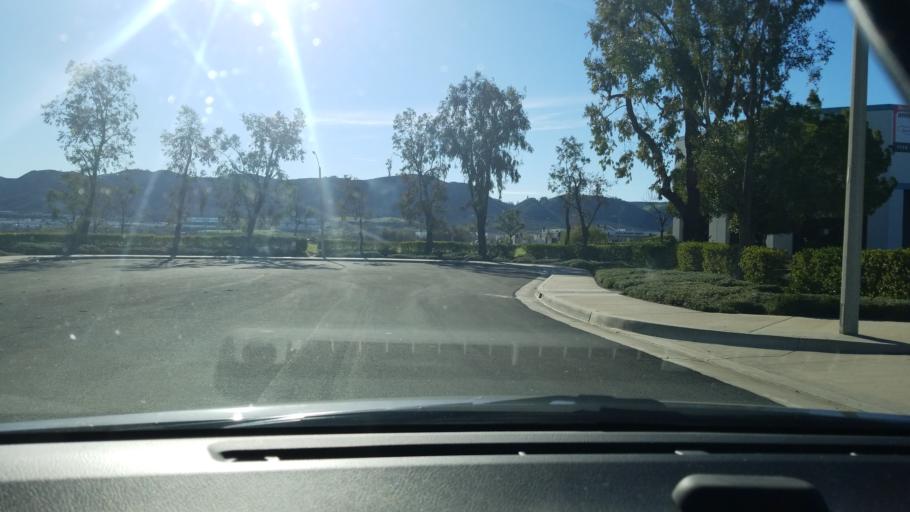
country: US
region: California
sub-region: Riverside County
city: Murrieta Hot Springs
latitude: 33.5279
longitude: -117.1698
